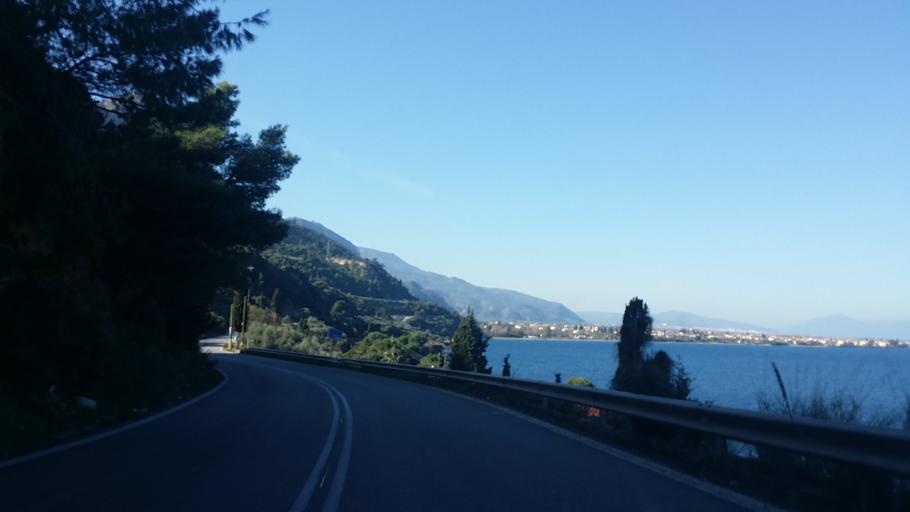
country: GR
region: West Greece
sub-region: Nomos Achaias
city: Akrata
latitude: 38.1782
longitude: 22.2284
